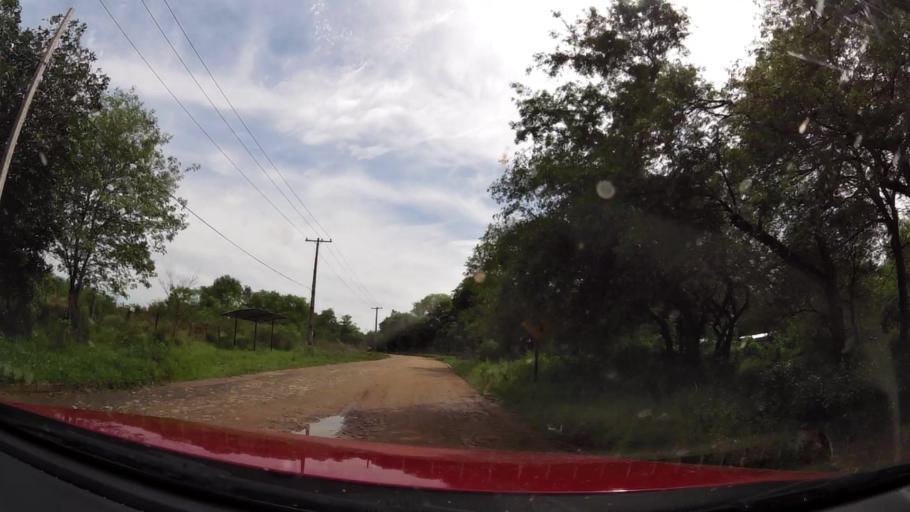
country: PY
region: Central
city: Limpio
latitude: -25.1883
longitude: -57.4741
